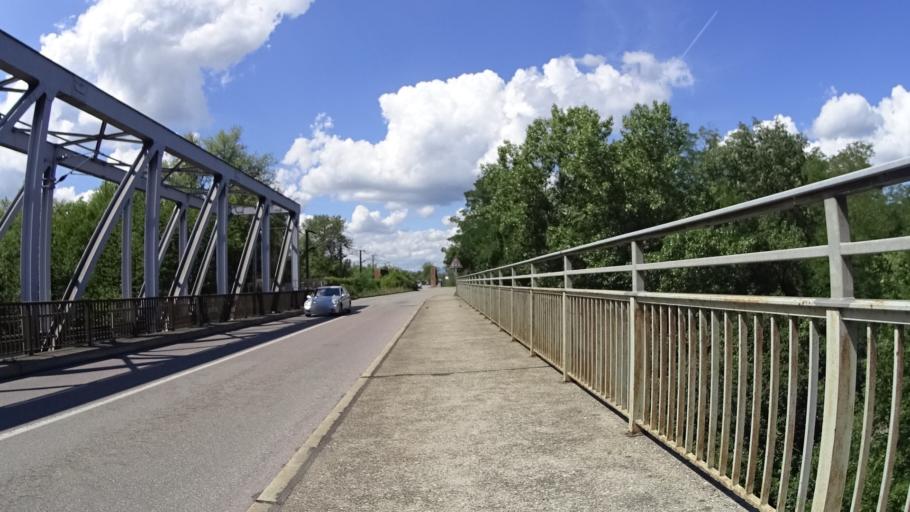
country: FR
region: Alsace
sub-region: Departement du Haut-Rhin
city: Chalampe
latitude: 47.8142
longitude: 7.5458
